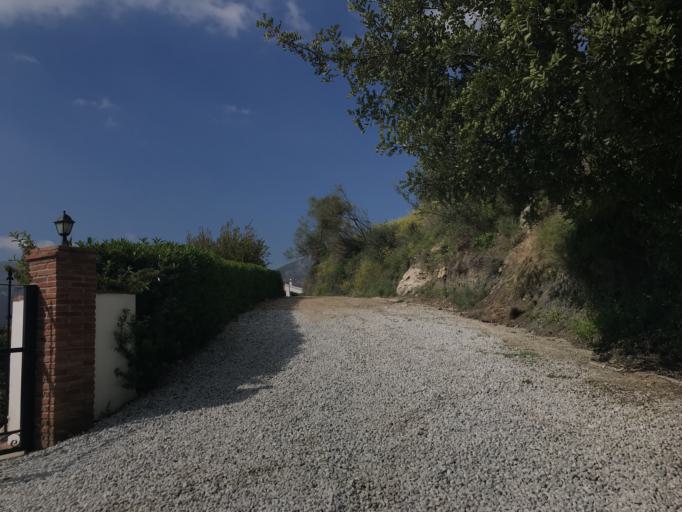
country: ES
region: Andalusia
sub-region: Provincia de Malaga
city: Alcaucin
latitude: 36.9080
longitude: -4.1096
